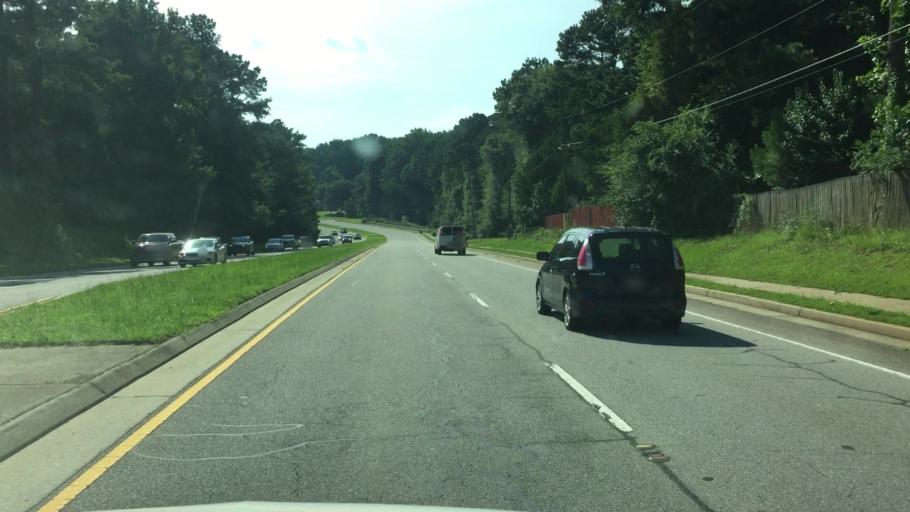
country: US
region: Georgia
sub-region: Gwinnett County
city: Grayson
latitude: 33.9184
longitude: -83.9791
